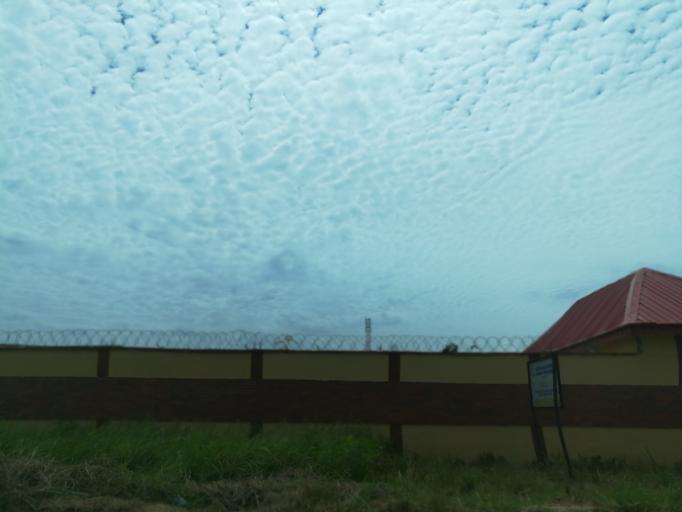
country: NG
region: Lagos
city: Ebute Ikorodu
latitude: 6.5576
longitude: 3.4758
